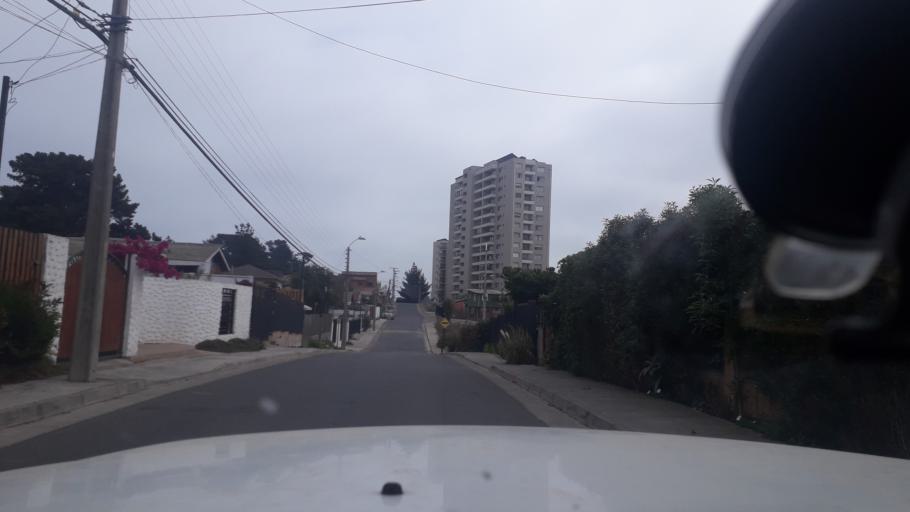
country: CL
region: Valparaiso
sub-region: Provincia de Valparaiso
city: Vina del Mar
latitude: -32.9380
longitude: -71.5313
